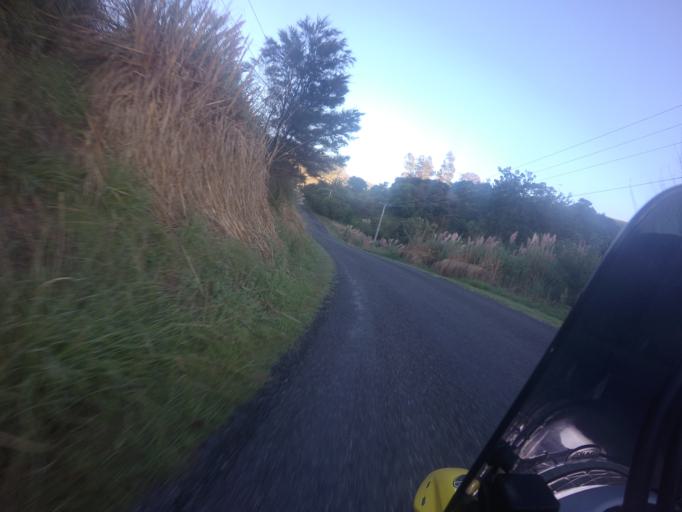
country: NZ
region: Gisborne
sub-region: Gisborne District
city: Gisborne
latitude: -38.6569
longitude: 178.0542
